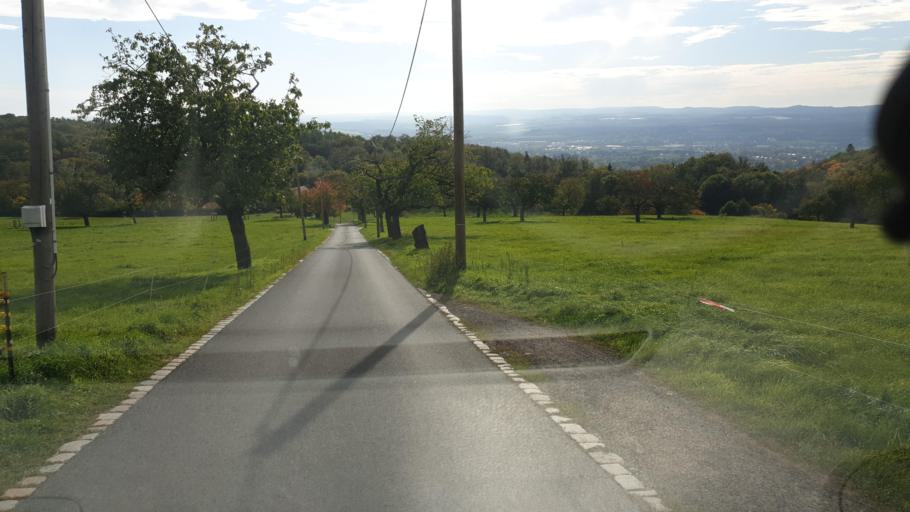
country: DE
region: Saxony
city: Heidenau
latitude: 51.0201
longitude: 13.8809
